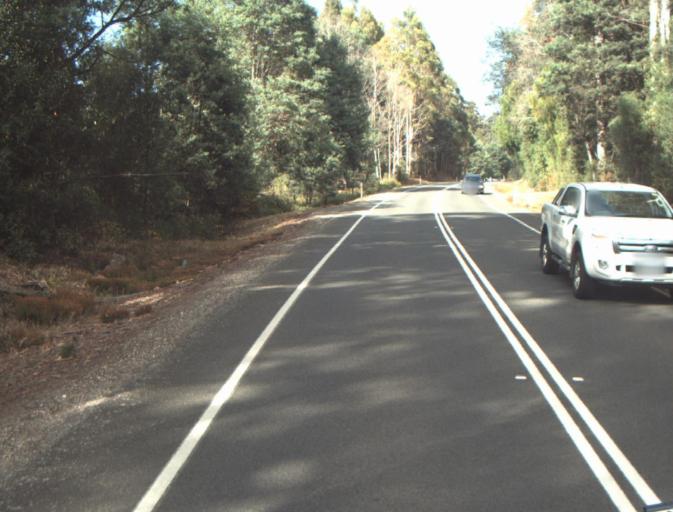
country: AU
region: Tasmania
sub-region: Launceston
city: Mayfield
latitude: -41.2975
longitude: 147.2118
